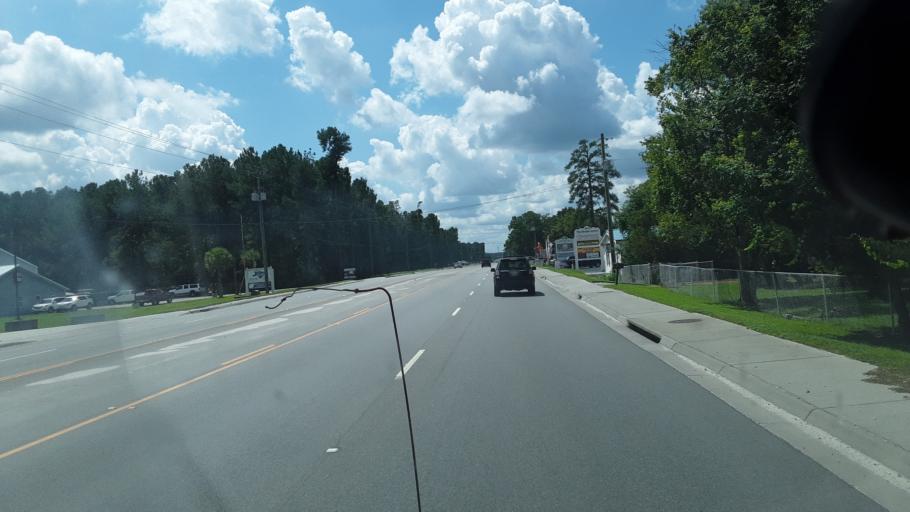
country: US
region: South Carolina
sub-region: Berkeley County
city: Sangaree
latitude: 33.0970
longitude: -80.0778
